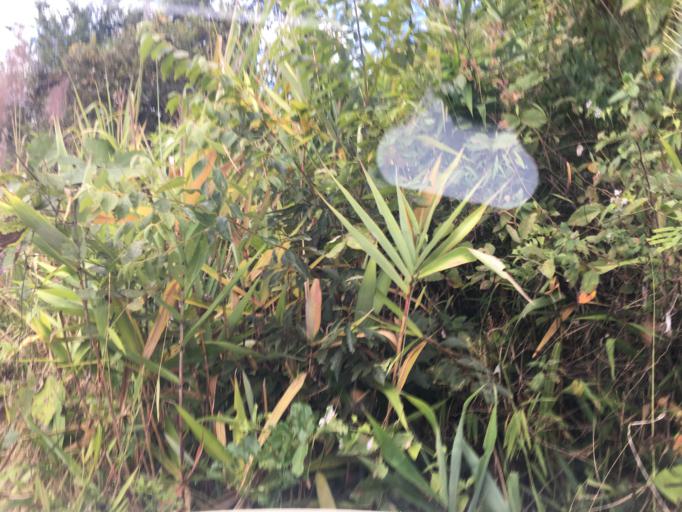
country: LA
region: Houaphan
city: Viengthong
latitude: 19.9123
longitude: 103.2986
